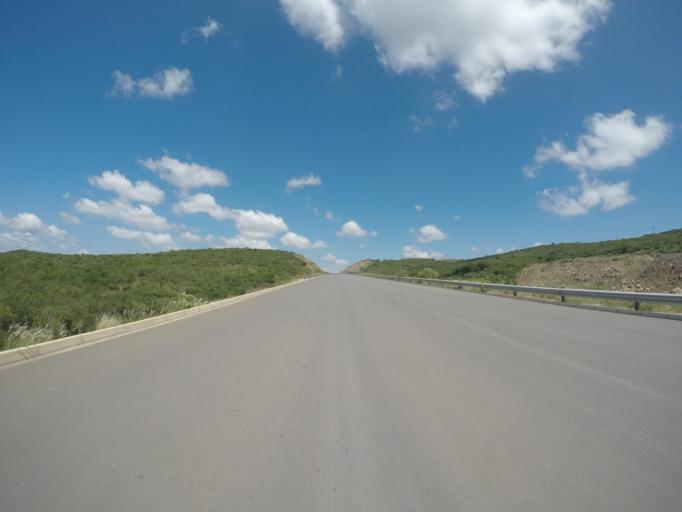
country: ZA
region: KwaZulu-Natal
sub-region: uThungulu District Municipality
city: Empangeni
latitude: -28.6241
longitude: 31.7577
